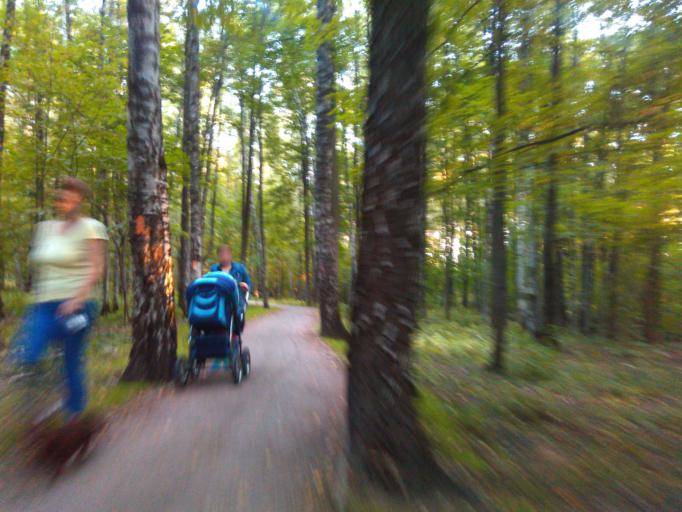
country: RU
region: Moscow
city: Troparevo
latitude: 55.6552
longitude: 37.5036
